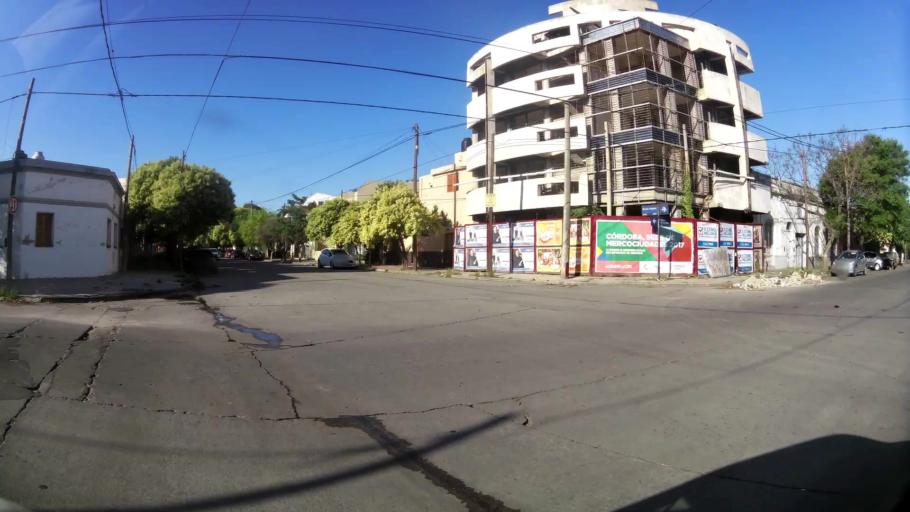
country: AR
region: Cordoba
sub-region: Departamento de Capital
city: Cordoba
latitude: -31.3897
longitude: -64.1769
